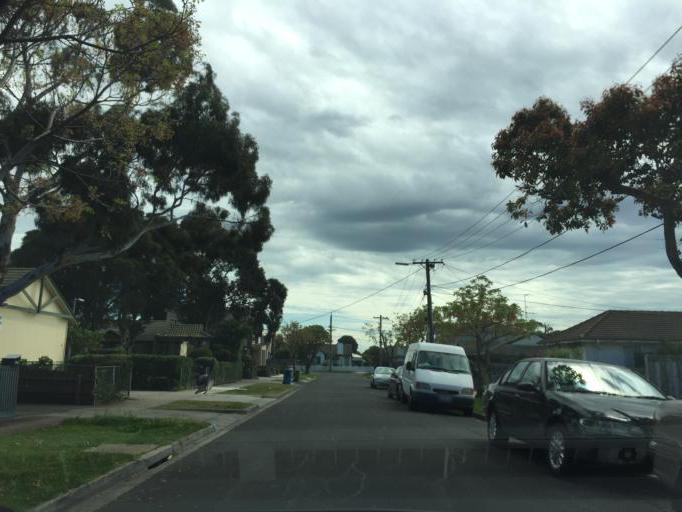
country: AU
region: Victoria
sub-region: Maribyrnong
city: Braybrook
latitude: -37.7894
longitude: 144.8591
